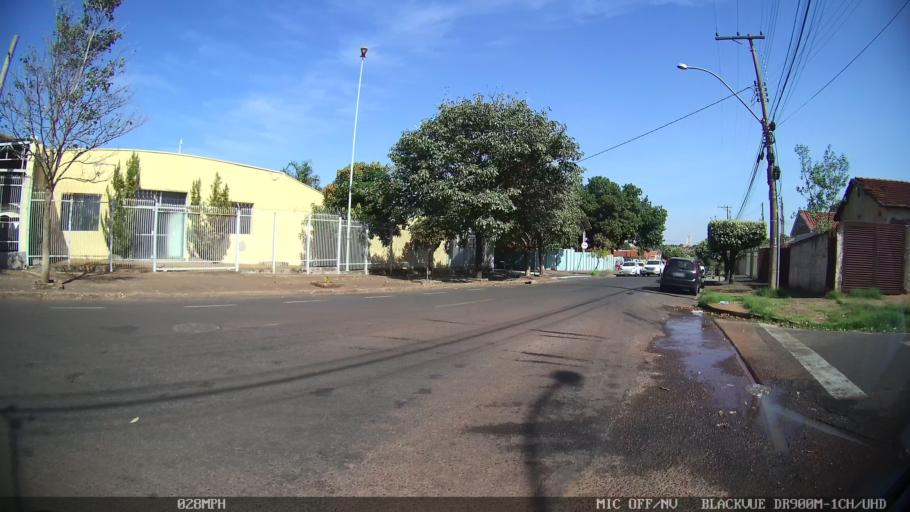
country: BR
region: Sao Paulo
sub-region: Sao Jose Do Rio Preto
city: Sao Jose do Rio Preto
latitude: -20.7888
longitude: -49.4043
